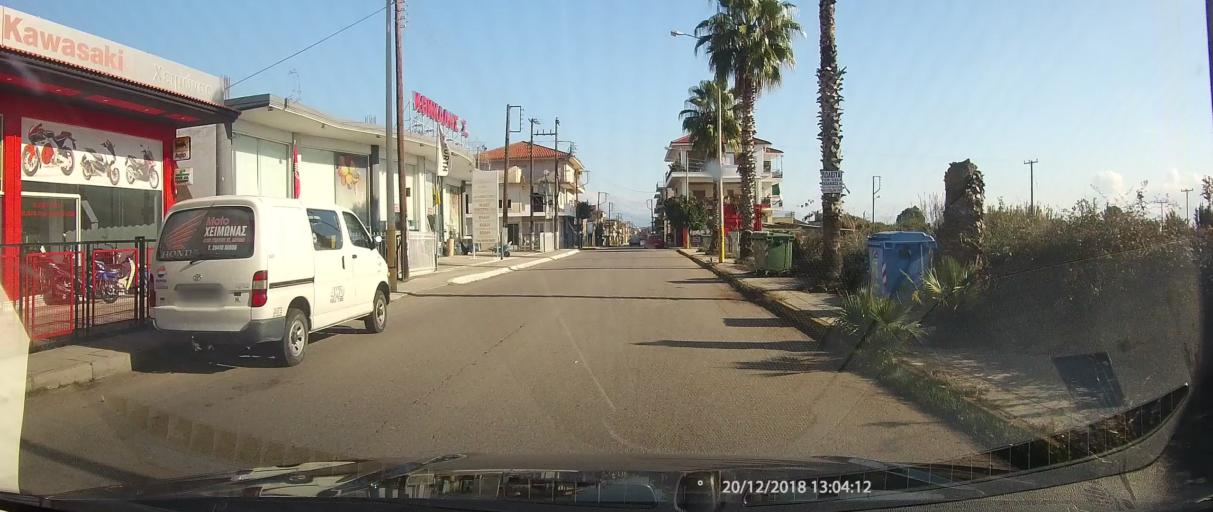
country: GR
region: West Greece
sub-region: Nomos Aitolias kai Akarnanias
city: Panaitolion
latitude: 38.5850
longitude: 21.4318
